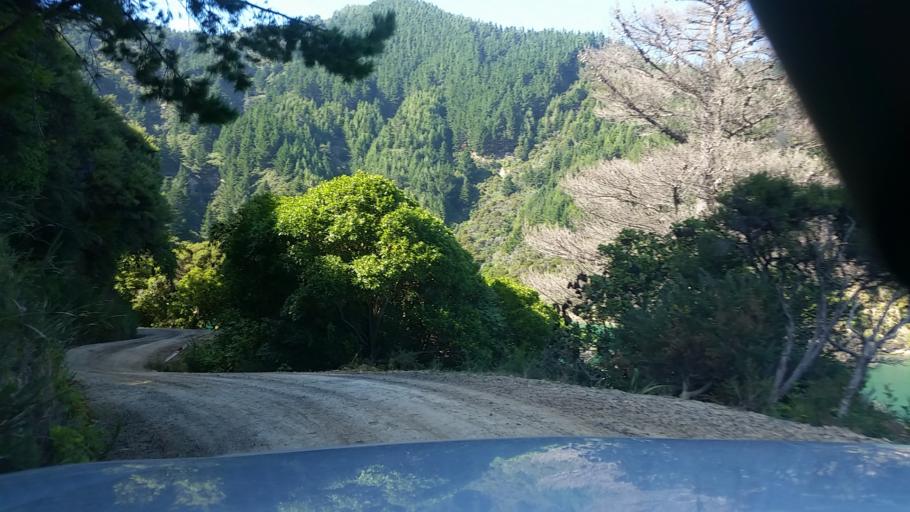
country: NZ
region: Marlborough
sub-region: Marlborough District
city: Picton
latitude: -41.3120
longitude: 174.1716
